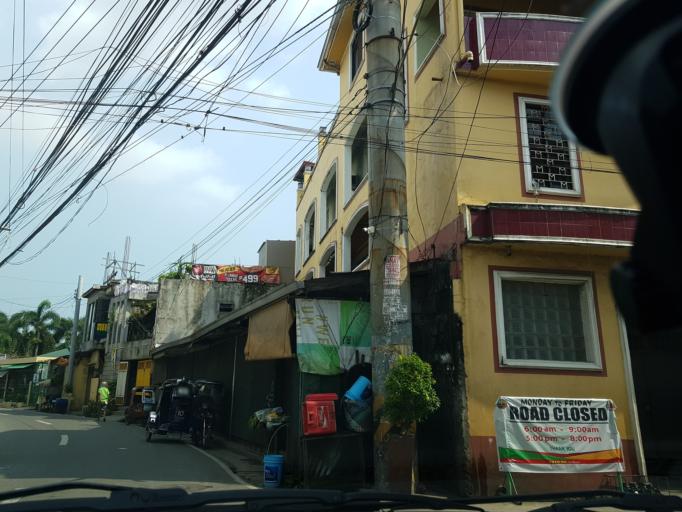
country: PH
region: Calabarzon
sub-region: Province of Rizal
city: Pateros
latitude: 14.5420
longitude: 121.0834
